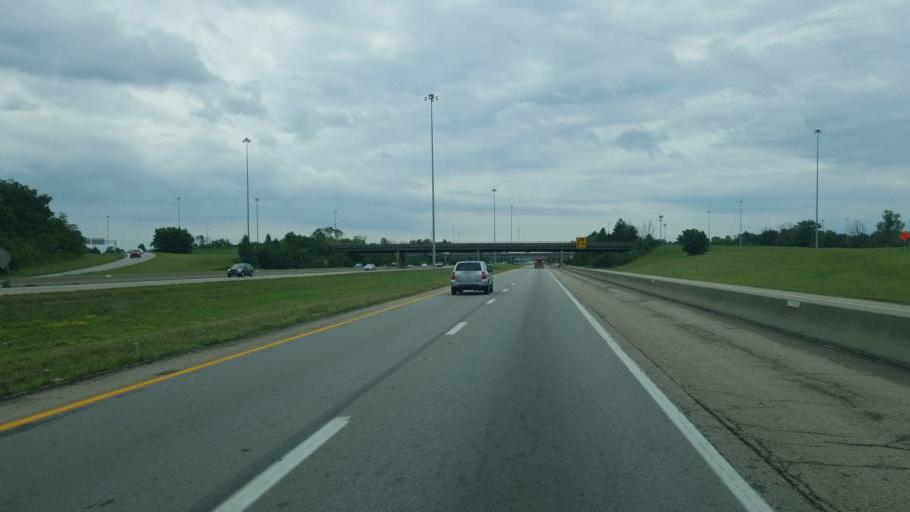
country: US
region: Ohio
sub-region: Franklin County
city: Grove City
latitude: 39.8945
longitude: -83.0434
